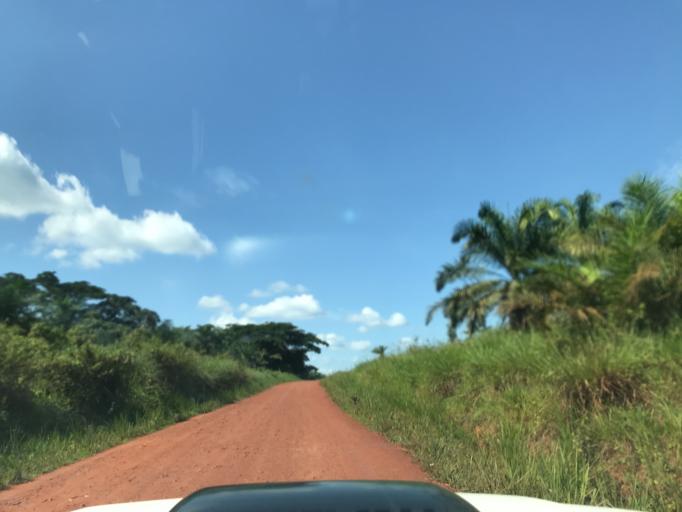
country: CD
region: Eastern Province
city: Kisangani
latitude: 1.2073
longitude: 25.2618
